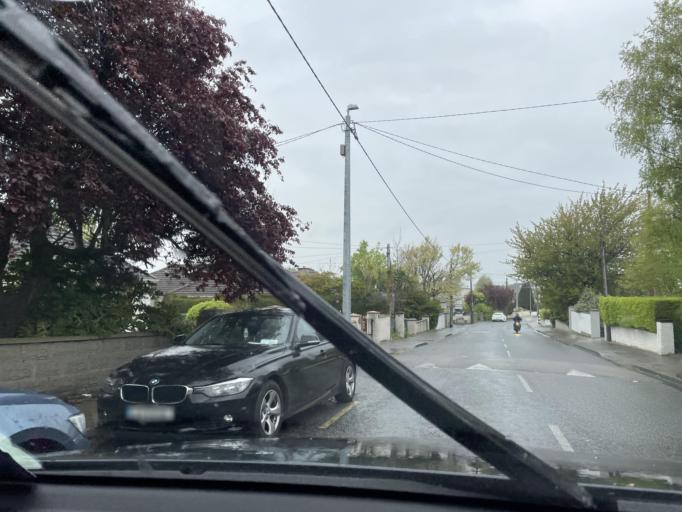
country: IE
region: Leinster
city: Dundrum
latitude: 53.2915
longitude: -6.2575
